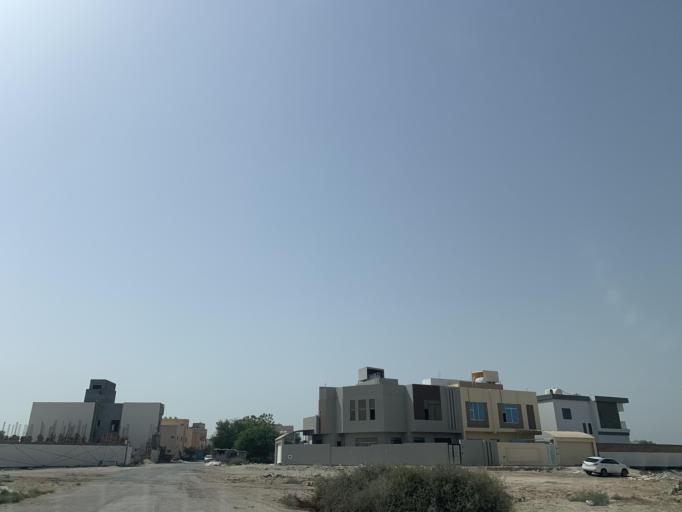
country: BH
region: Manama
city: Jidd Hafs
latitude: 26.2098
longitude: 50.5157
